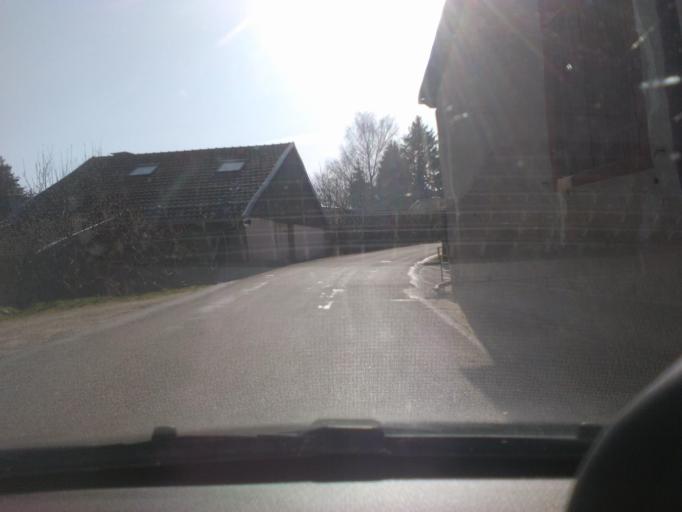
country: FR
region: Lorraine
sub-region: Departement des Vosges
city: Ban-de-Laveline
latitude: 48.3400
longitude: 7.0710
